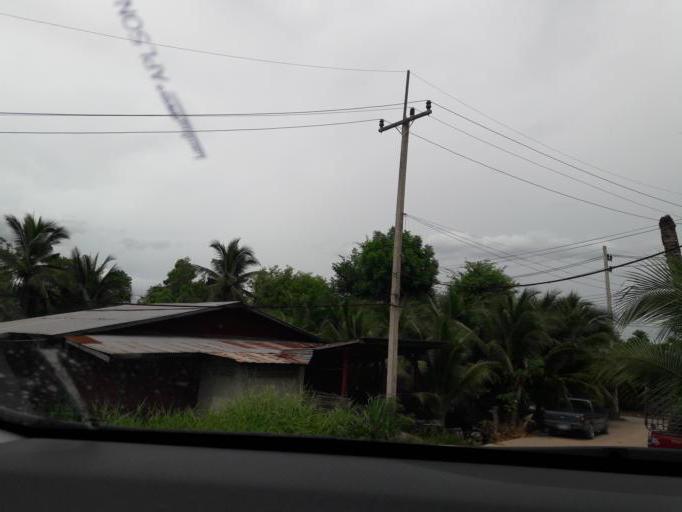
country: TH
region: Ratchaburi
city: Damnoen Saduak
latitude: 13.5364
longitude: 100.0392
